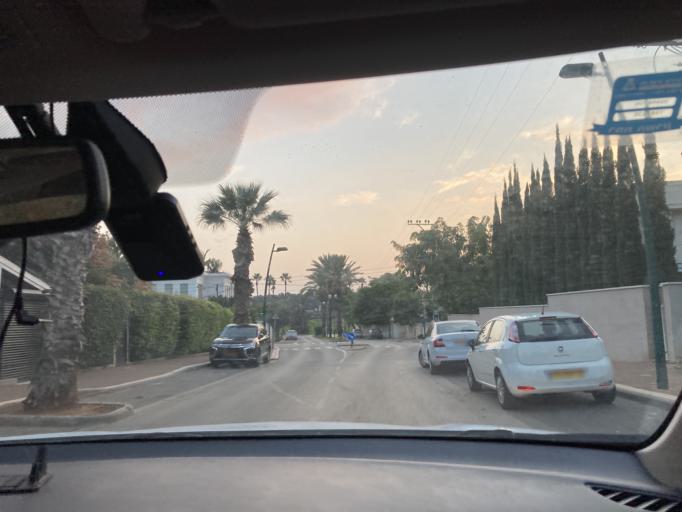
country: IL
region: Tel Aviv
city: Ramat HaSharon
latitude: 32.1495
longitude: 34.8279
